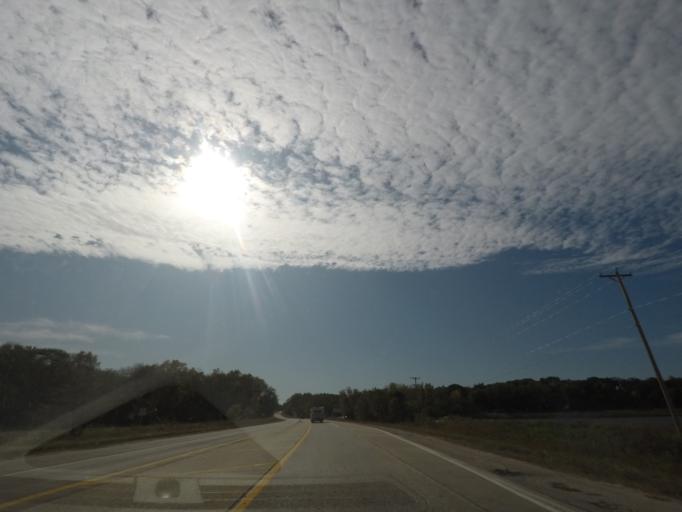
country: US
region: Iowa
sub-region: Story County
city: Ames
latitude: 42.0653
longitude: -93.6231
